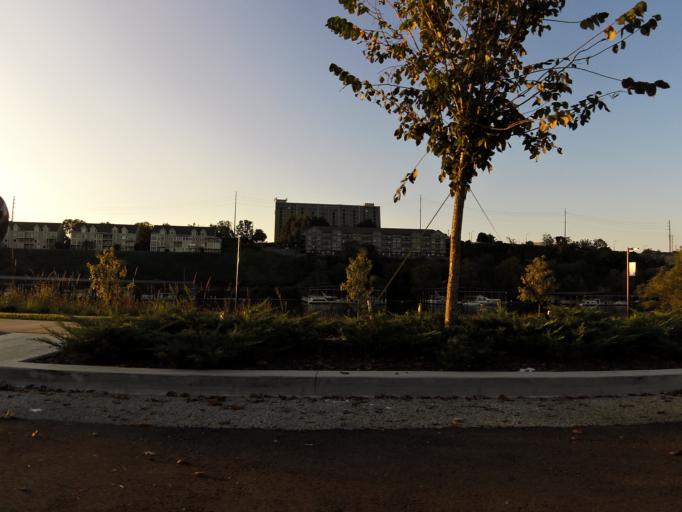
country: US
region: Tennessee
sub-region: Knox County
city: Knoxville
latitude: 35.9607
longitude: -83.9078
